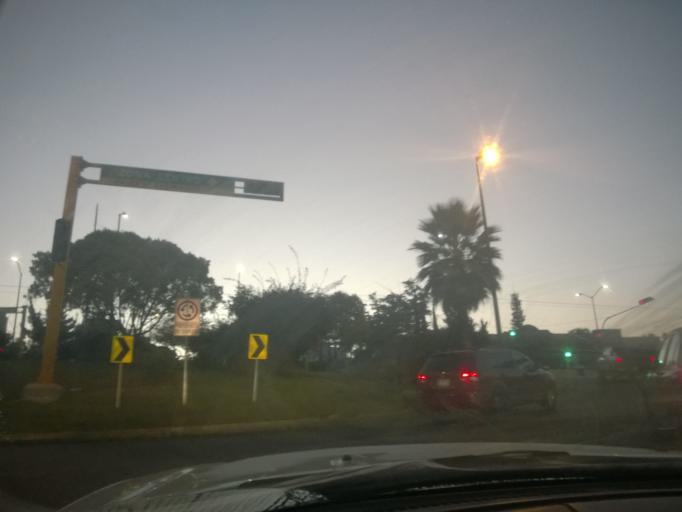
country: MX
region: Guanajuato
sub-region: Leon
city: La Ermita
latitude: 21.1519
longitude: -101.7209
